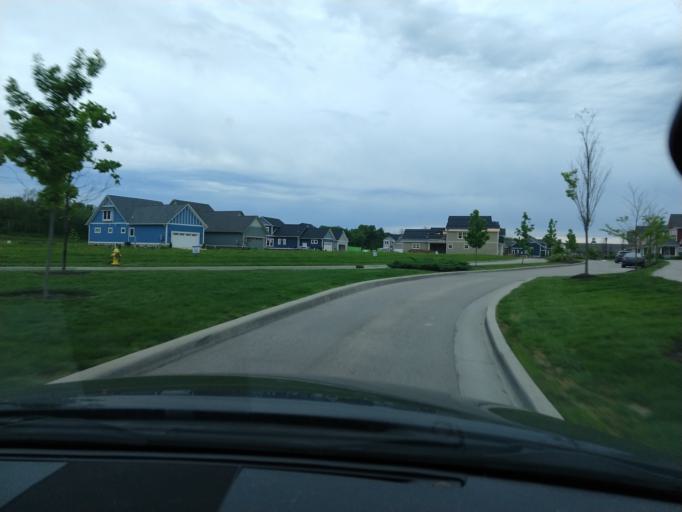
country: US
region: Indiana
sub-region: Hamilton County
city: Carmel
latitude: 39.9321
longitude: -86.1315
